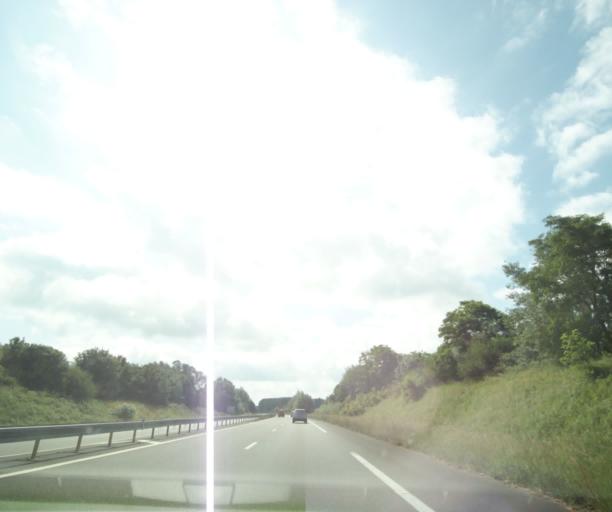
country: FR
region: Pays de la Loire
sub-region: Departement de Maine-et-Loire
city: Jumelles
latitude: 47.3912
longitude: -0.1061
